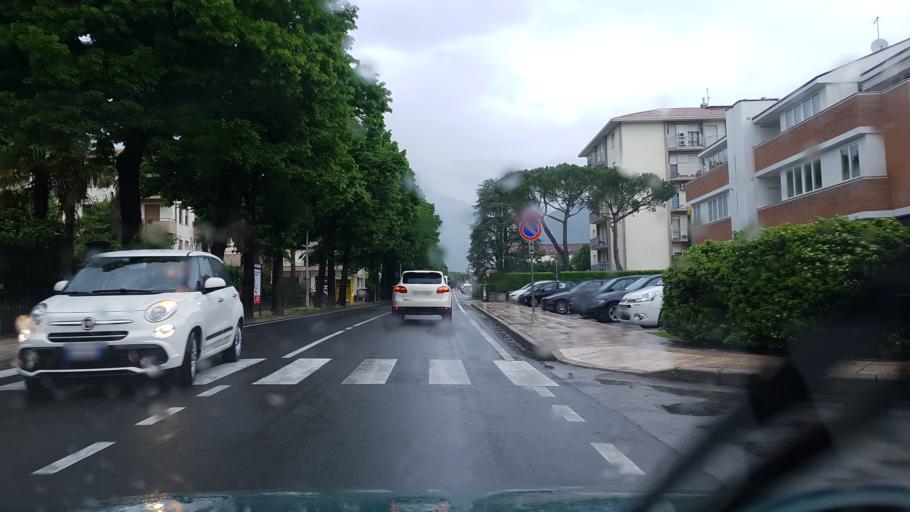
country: IT
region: Veneto
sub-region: Provincia di Treviso
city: Vittorio Veneto
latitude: 45.9824
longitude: 12.3038
